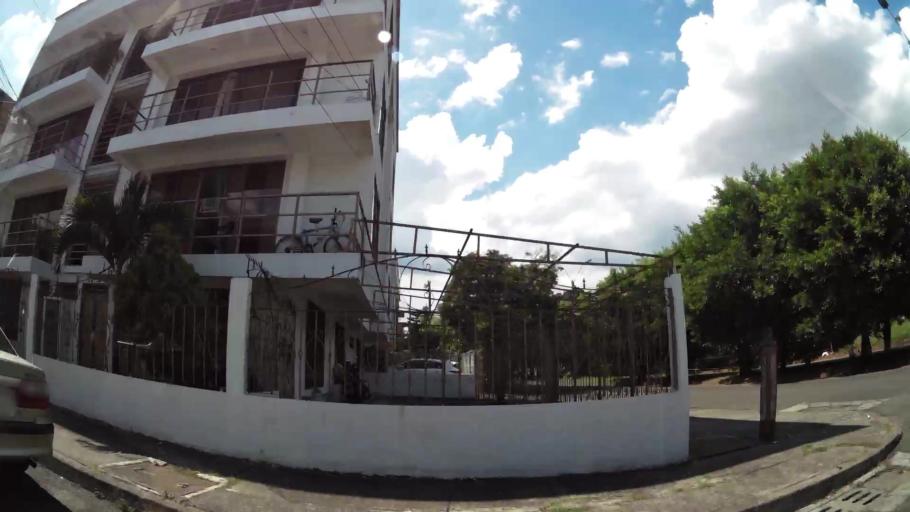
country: CO
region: Valle del Cauca
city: Cali
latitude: 3.3976
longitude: -76.5176
